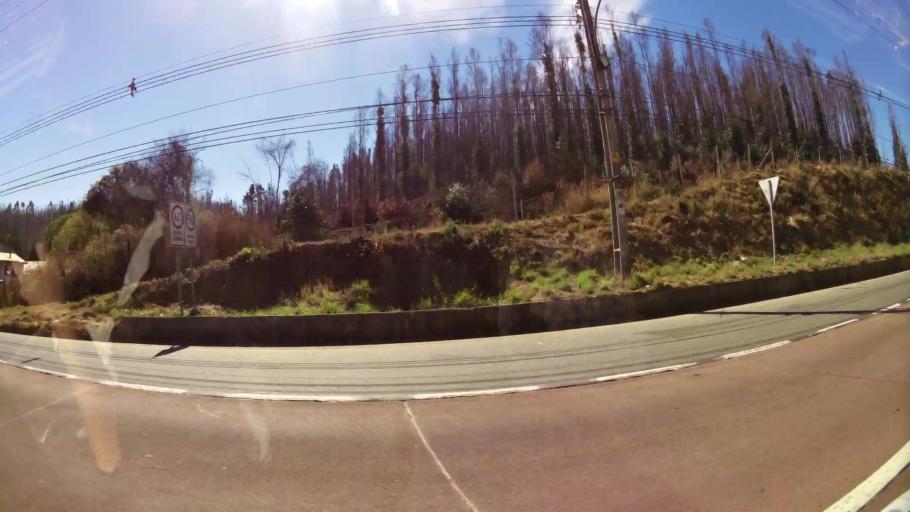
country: CL
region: Biobio
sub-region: Provincia de Concepcion
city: Penco
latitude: -36.7571
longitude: -73.0034
